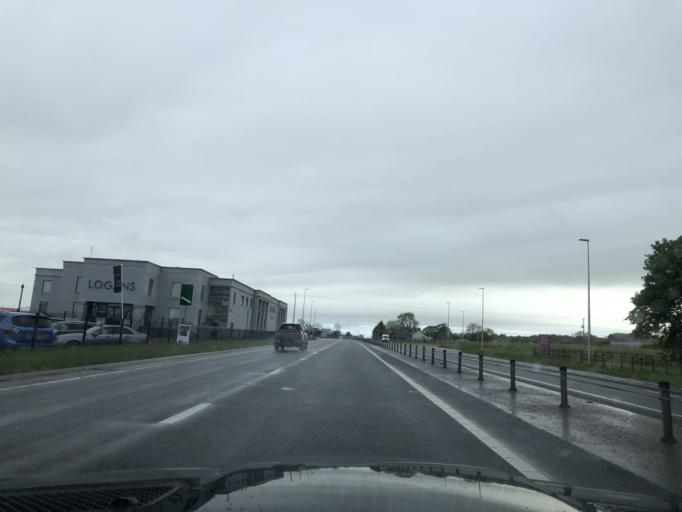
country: GB
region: Northern Ireland
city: Dunloy
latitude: 55.0025
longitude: -6.3576
